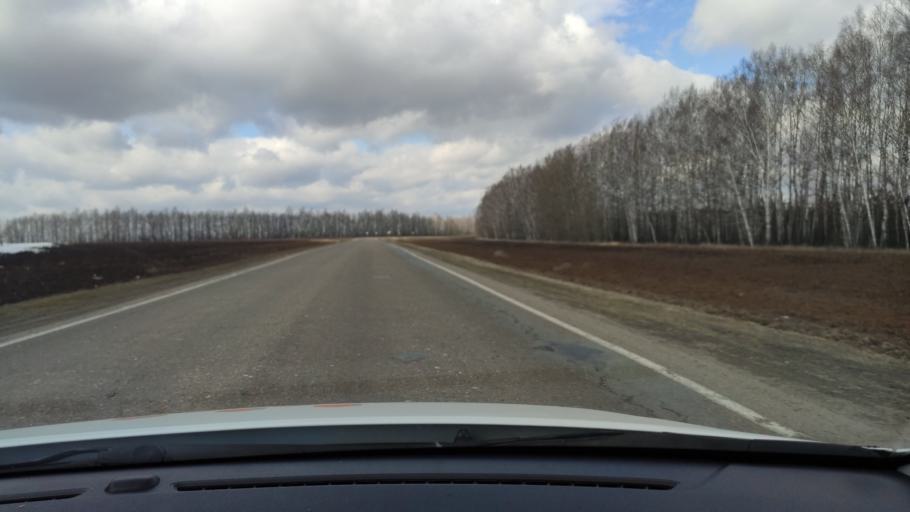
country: RU
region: Tatarstan
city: Vysokaya Gora
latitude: 56.0926
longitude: 49.1815
